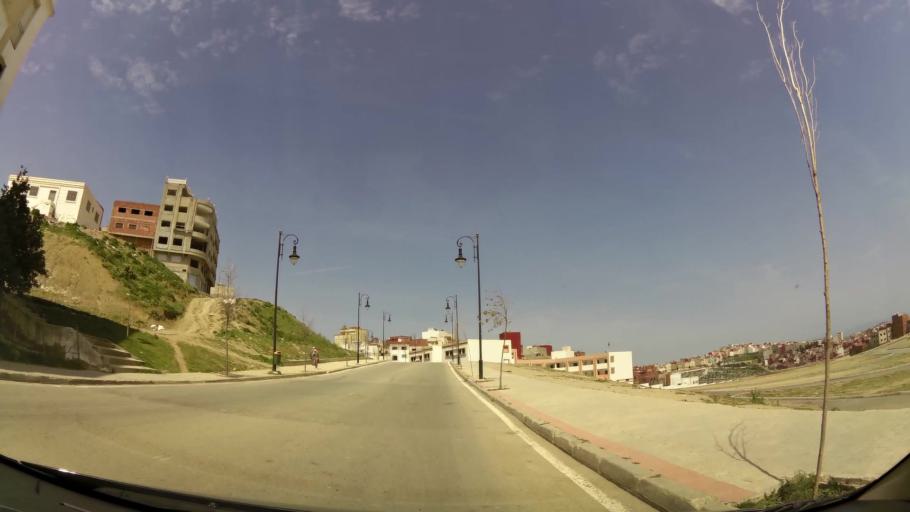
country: MA
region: Tanger-Tetouan
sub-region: Tanger-Assilah
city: Tangier
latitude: 35.7338
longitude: -5.8159
